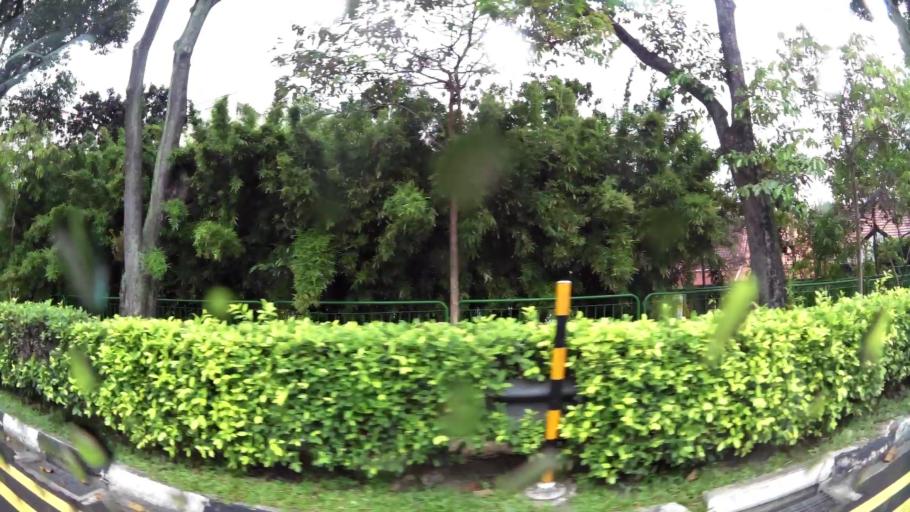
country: SG
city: Singapore
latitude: 1.3585
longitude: 103.8740
